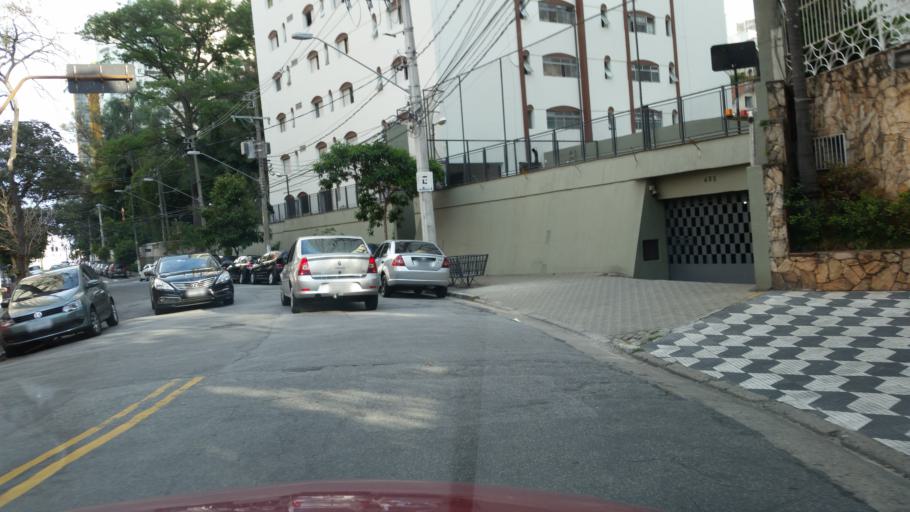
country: BR
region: Sao Paulo
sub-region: Sao Paulo
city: Sao Paulo
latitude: -23.5646
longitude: -46.6445
